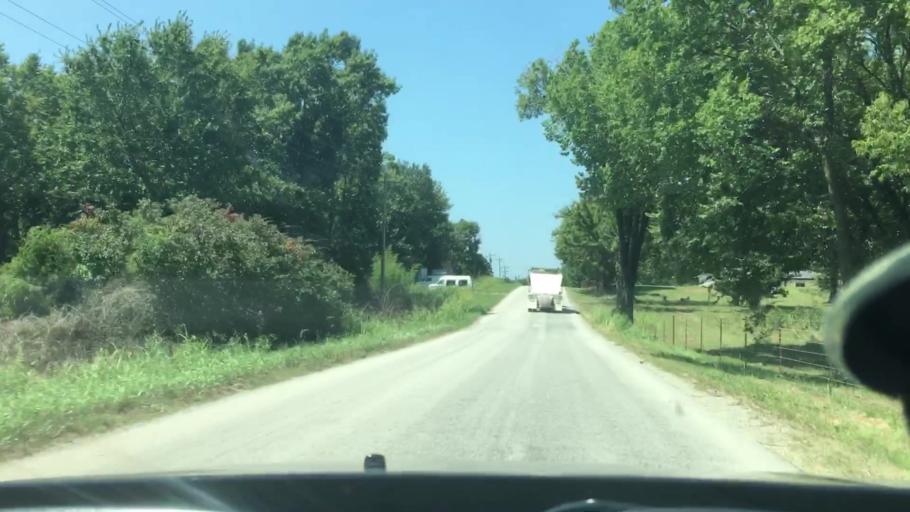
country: US
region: Oklahoma
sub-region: Johnston County
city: Tishomingo
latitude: 34.2588
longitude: -96.4206
